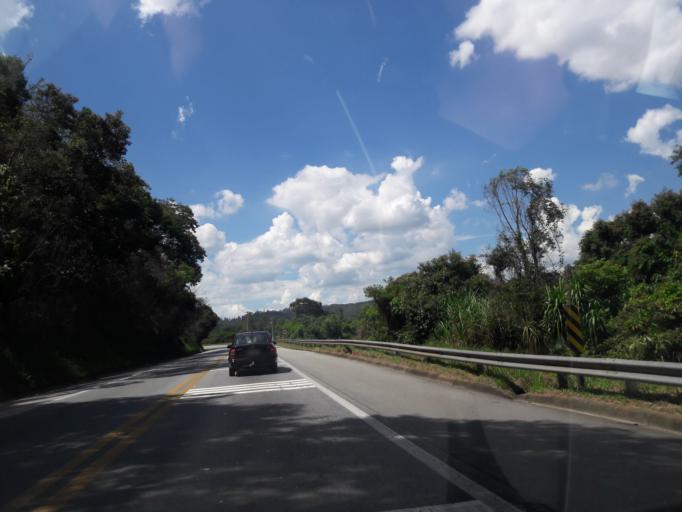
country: BR
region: Sao Paulo
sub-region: Francisco Morato
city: Francisco Morato
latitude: -23.2952
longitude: -46.8062
